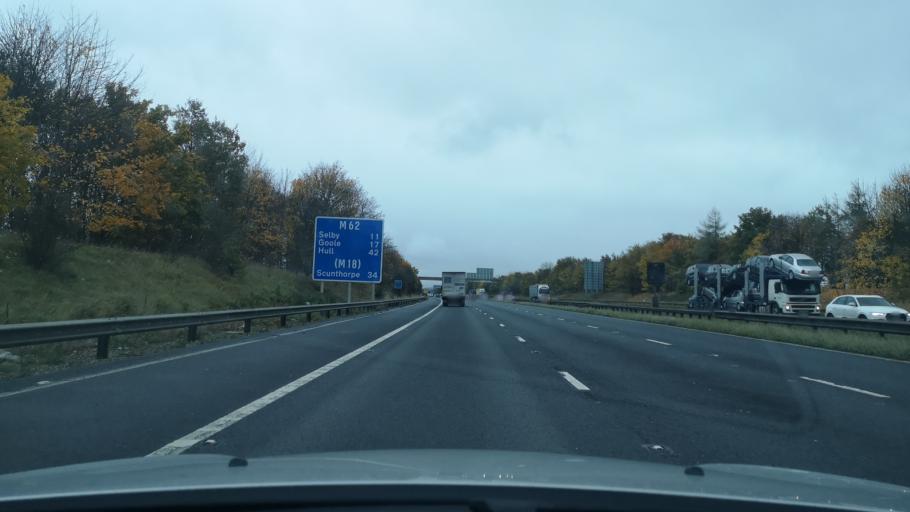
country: GB
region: England
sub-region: City and Borough of Wakefield
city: Knottingley
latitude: 53.6930
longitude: -1.2488
